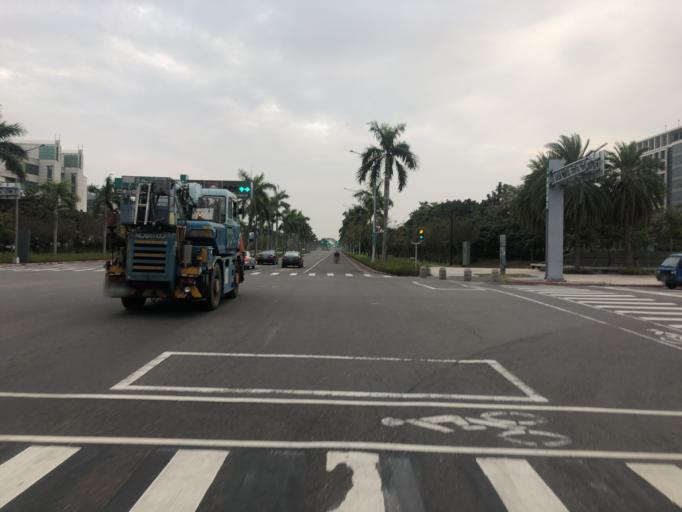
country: TW
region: Taiwan
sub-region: Tainan
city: Tainan
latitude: 23.0990
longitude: 120.2808
